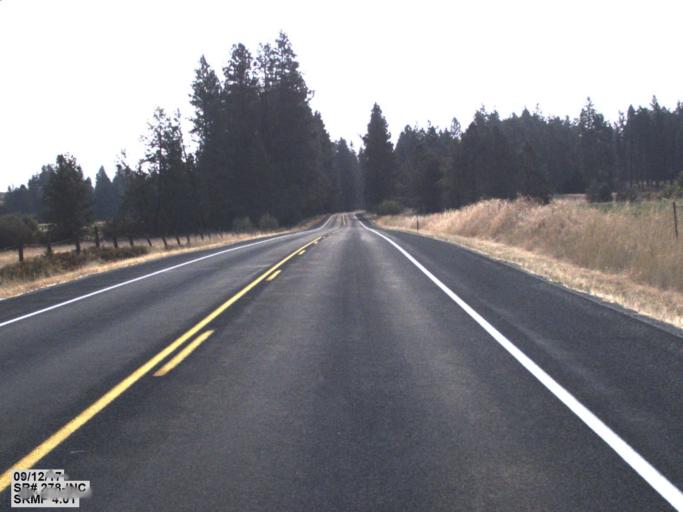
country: US
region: Idaho
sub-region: Benewah County
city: Plummer
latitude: 47.4429
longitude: -117.0688
